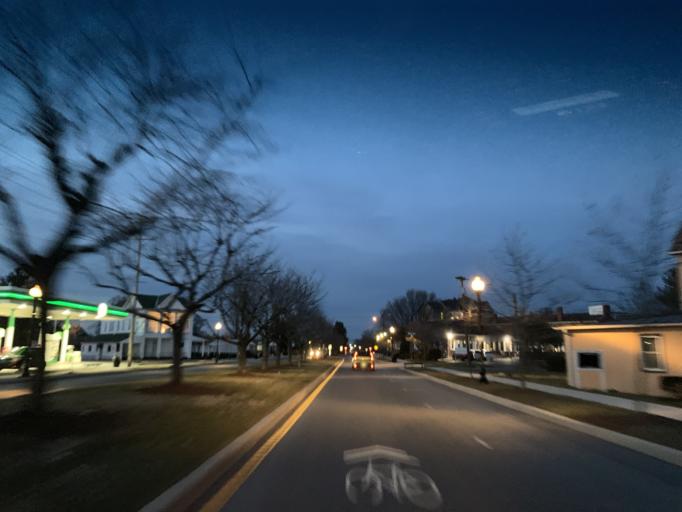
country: US
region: West Virginia
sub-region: Jefferson County
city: Ranson
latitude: 39.2930
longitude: -77.8613
